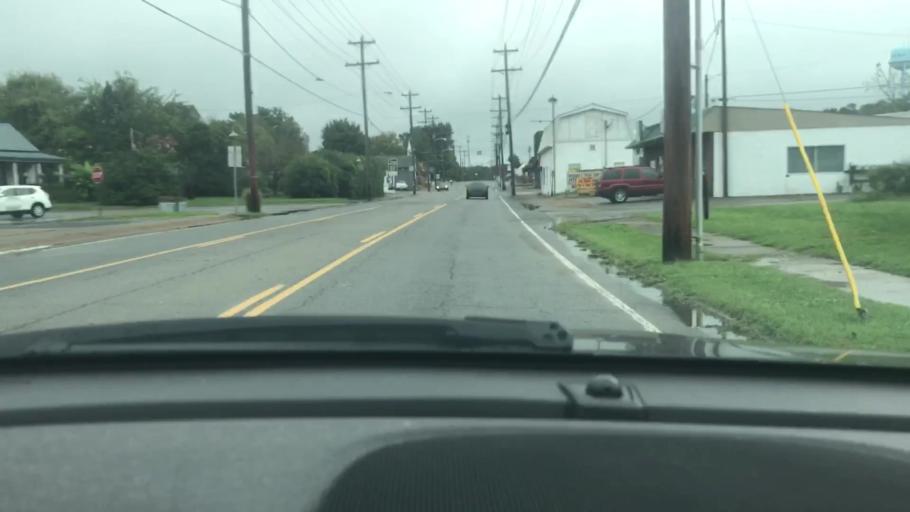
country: US
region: Tennessee
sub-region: Dickson County
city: White Bluff
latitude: 36.1077
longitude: -87.2218
